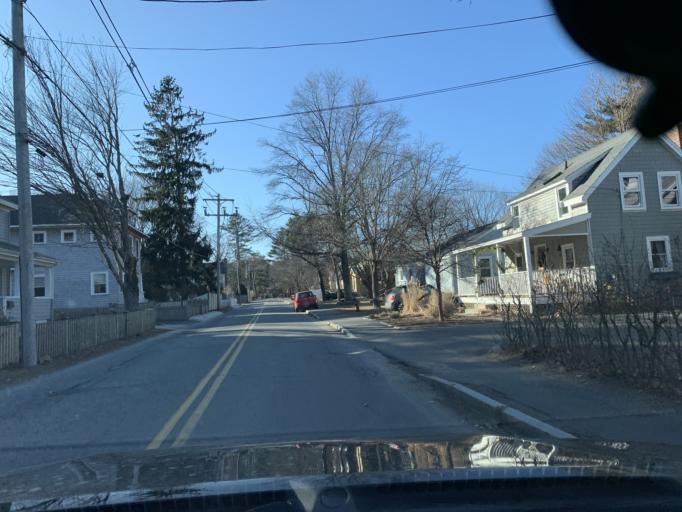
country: US
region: Massachusetts
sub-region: Essex County
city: Essex
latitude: 42.5834
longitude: -70.7778
